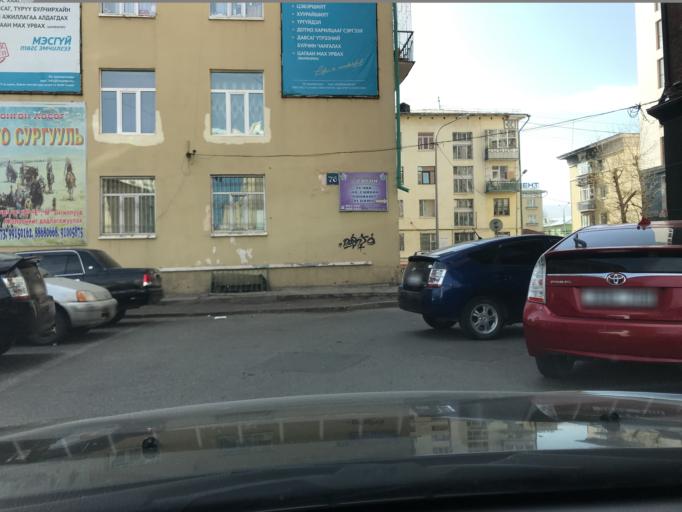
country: MN
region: Ulaanbaatar
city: Ulaanbaatar
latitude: 47.9170
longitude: 106.9054
